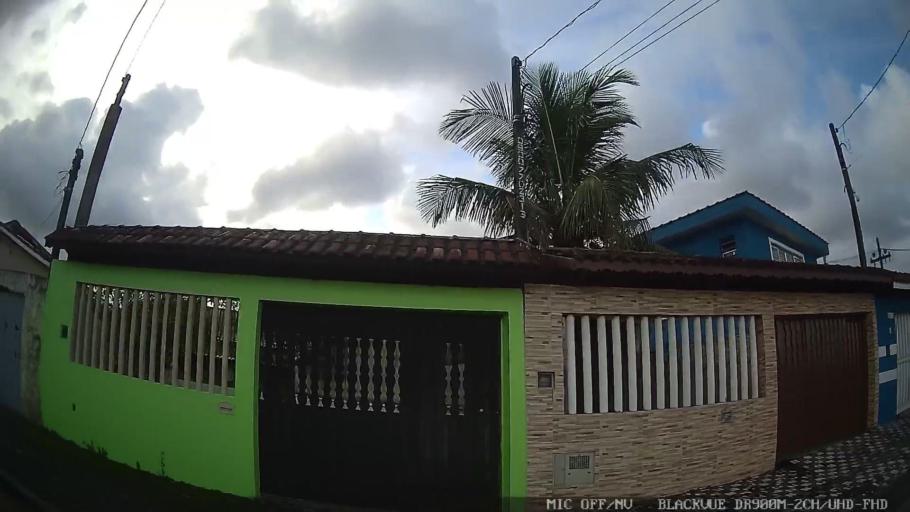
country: BR
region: Sao Paulo
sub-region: Mongagua
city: Mongagua
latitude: -24.1174
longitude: -46.6740
